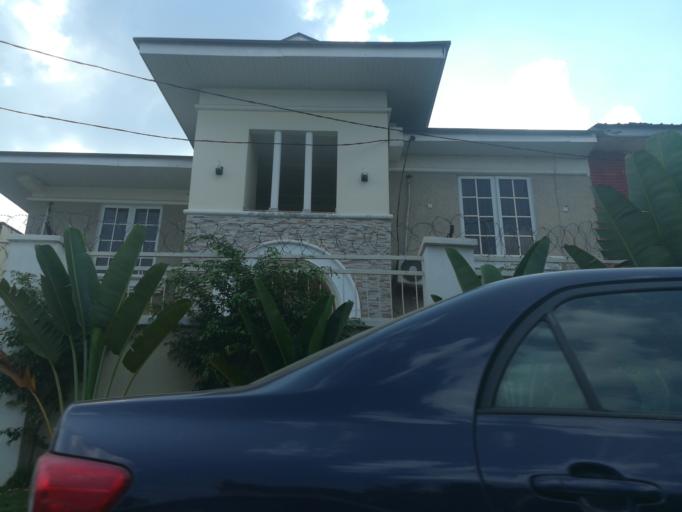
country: NG
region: Abuja Federal Capital Territory
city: Abuja
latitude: 9.0852
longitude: 7.4150
